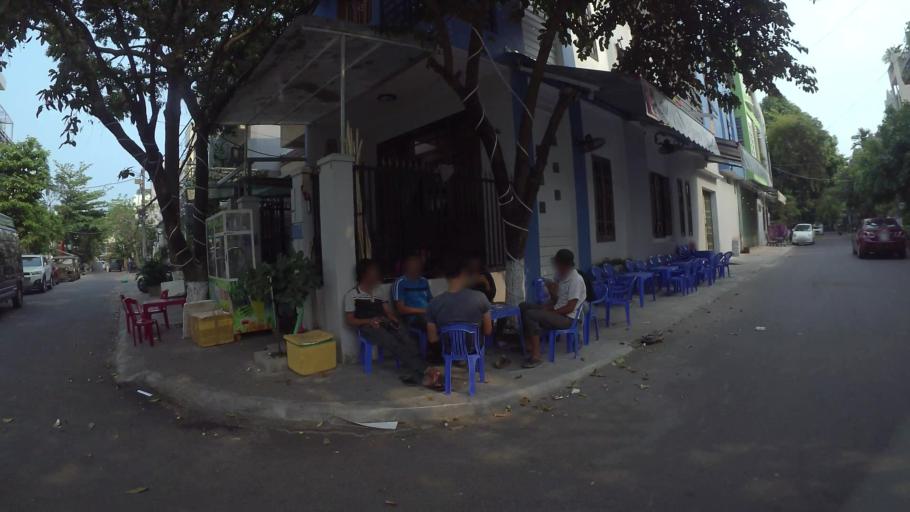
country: VN
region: Da Nang
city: Son Tra
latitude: 16.0447
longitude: 108.2193
